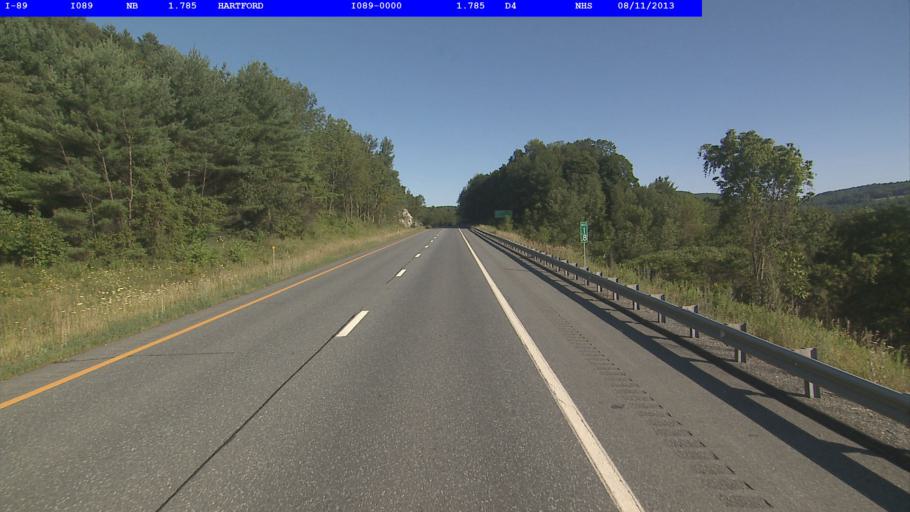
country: US
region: Vermont
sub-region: Windsor County
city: White River Junction
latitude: 43.6548
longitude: -72.3484
